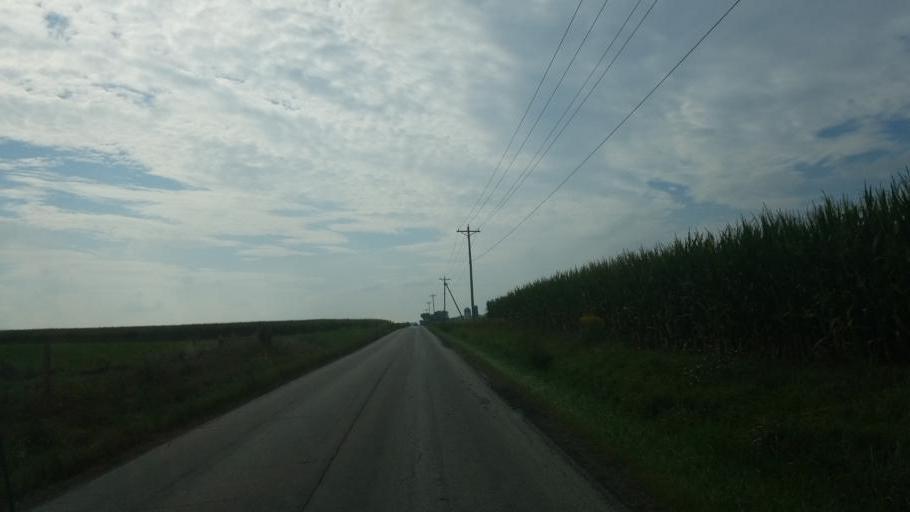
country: US
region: Ohio
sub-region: Wayne County
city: West Salem
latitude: 40.9159
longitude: -82.0252
